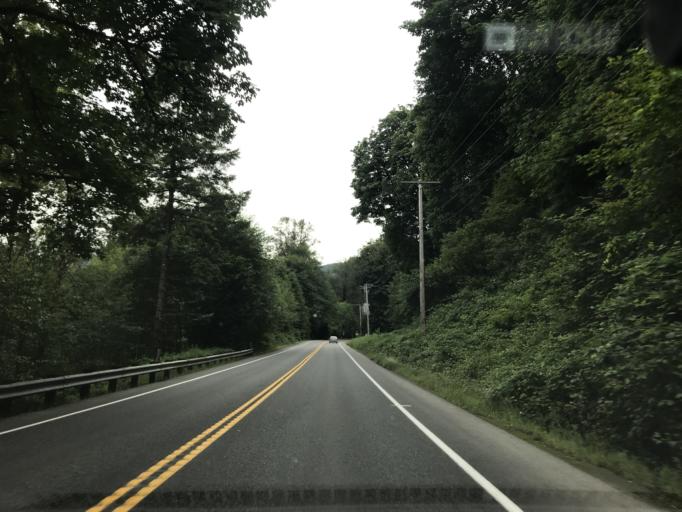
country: US
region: Washington
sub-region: King County
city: Fall City
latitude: 47.5291
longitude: -121.9228
